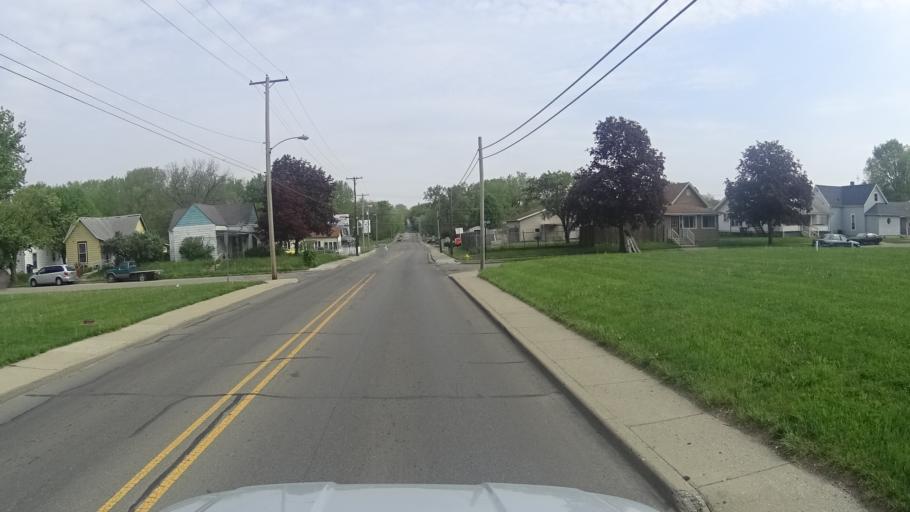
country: US
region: Indiana
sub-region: Madison County
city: Anderson
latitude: 40.1141
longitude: -85.6918
